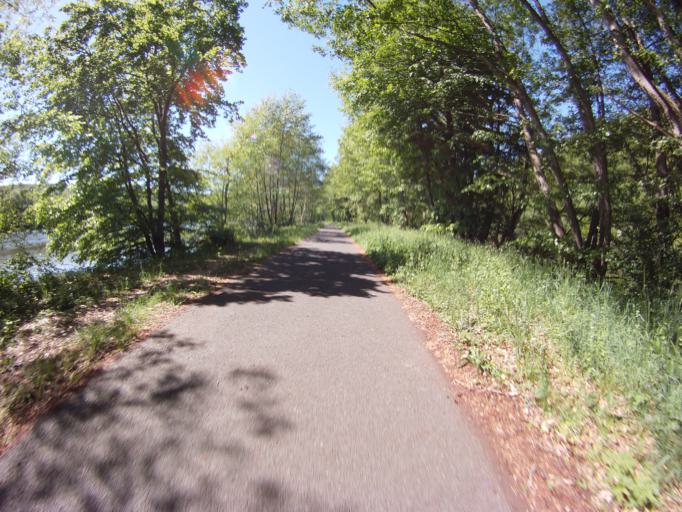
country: FR
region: Lorraine
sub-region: Departement de Meurthe-et-Moselle
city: Velaine-en-Haye
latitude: 48.6595
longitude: 6.0057
